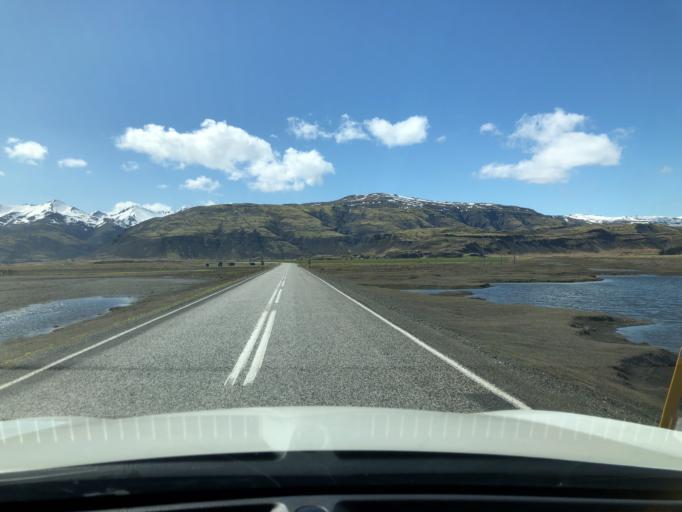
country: IS
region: East
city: Hoefn
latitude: 64.4199
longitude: -14.8879
